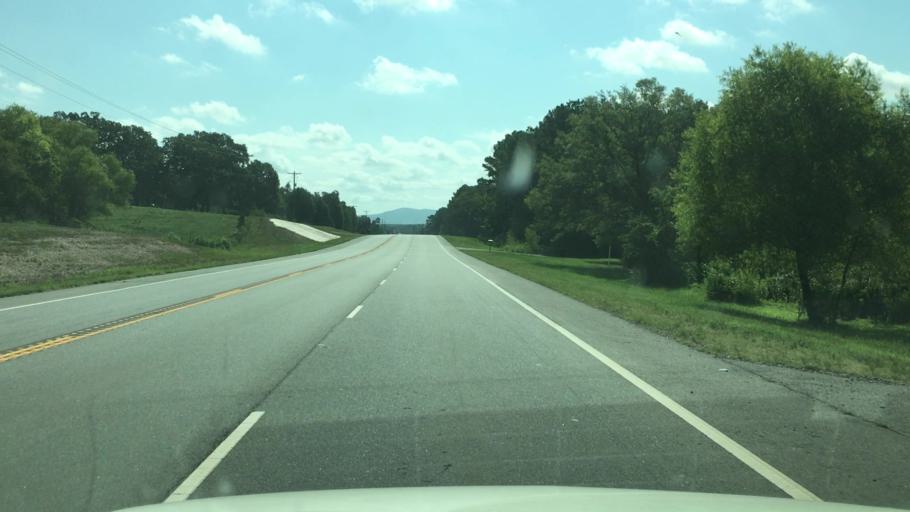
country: US
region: Arkansas
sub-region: Garland County
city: Piney
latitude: 34.5112
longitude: -93.2344
